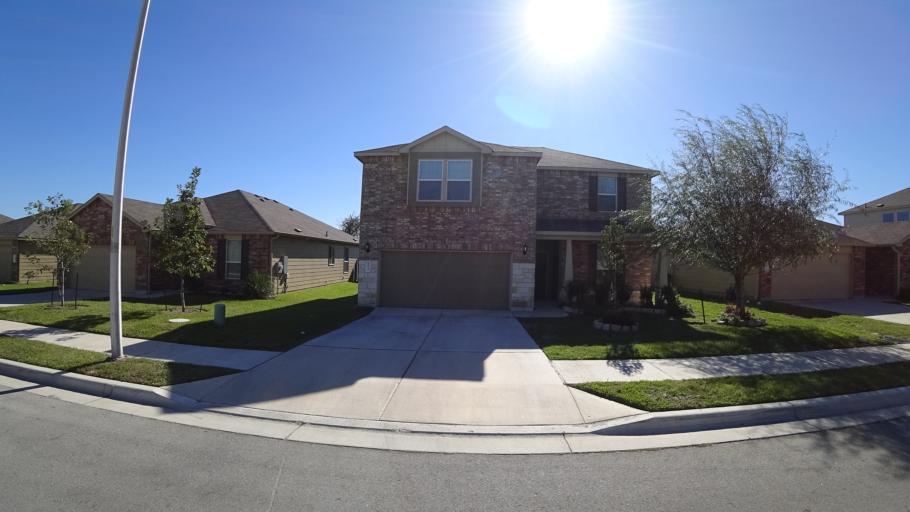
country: US
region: Texas
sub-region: Travis County
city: Hornsby Bend
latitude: 30.2787
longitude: -97.6241
